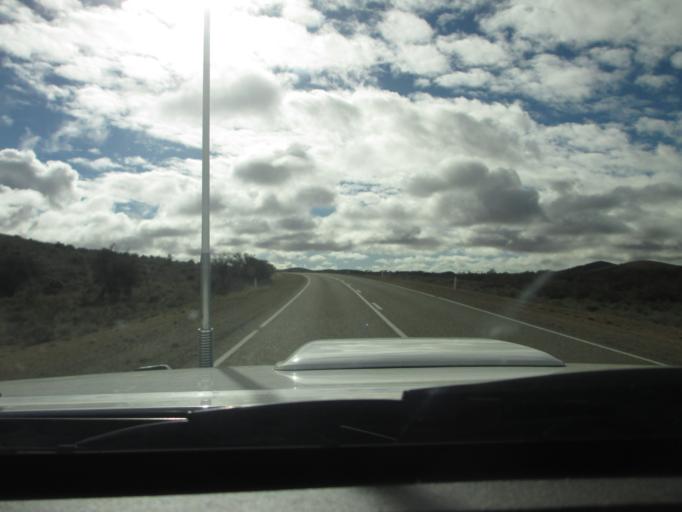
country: AU
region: South Australia
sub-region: Flinders Ranges
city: Quorn
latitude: -32.2051
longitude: 138.5277
